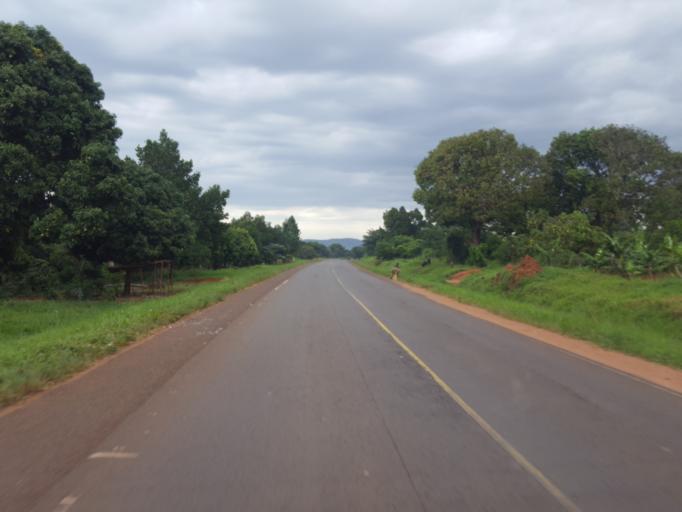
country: UG
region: Central Region
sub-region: Kiboga District
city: Kiboga
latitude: 0.8765
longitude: 31.8481
